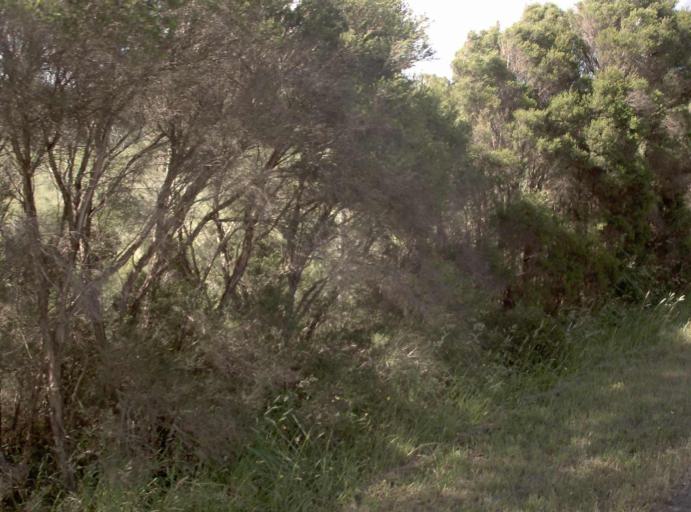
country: AU
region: Victoria
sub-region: Latrobe
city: Morwell
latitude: -38.1698
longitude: 146.4099
